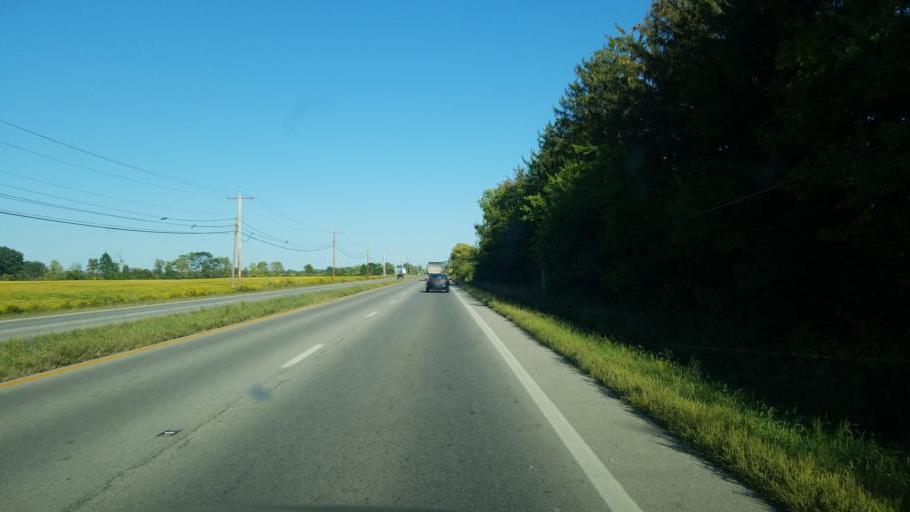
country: US
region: Ohio
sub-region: Franklin County
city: Lake Darby
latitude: 39.9481
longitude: -83.2247
